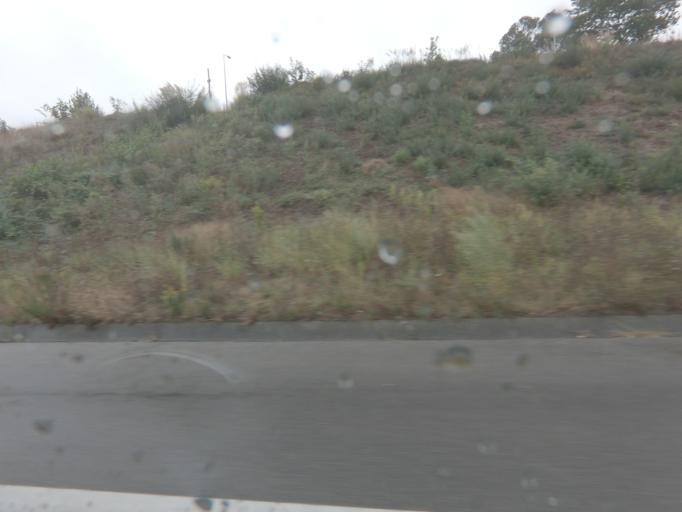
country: PT
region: Porto
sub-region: Matosinhos
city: Guifoes
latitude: 41.1992
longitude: -8.6599
